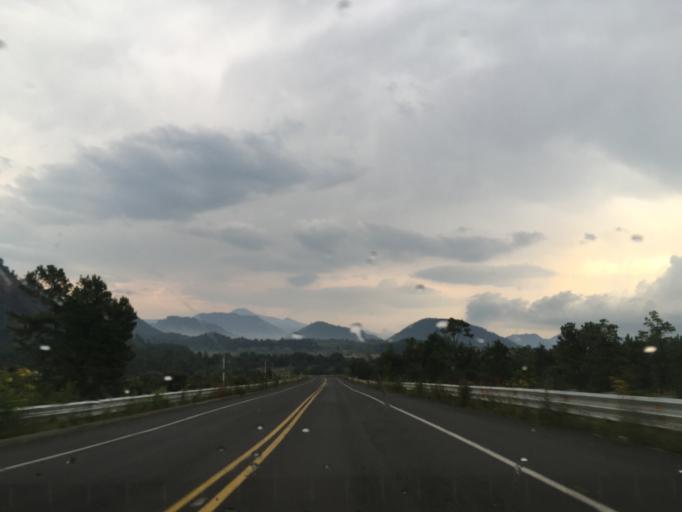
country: MX
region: Michoacan
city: Nuevo San Juan Parangaricutiro
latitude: 19.5040
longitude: -102.1343
